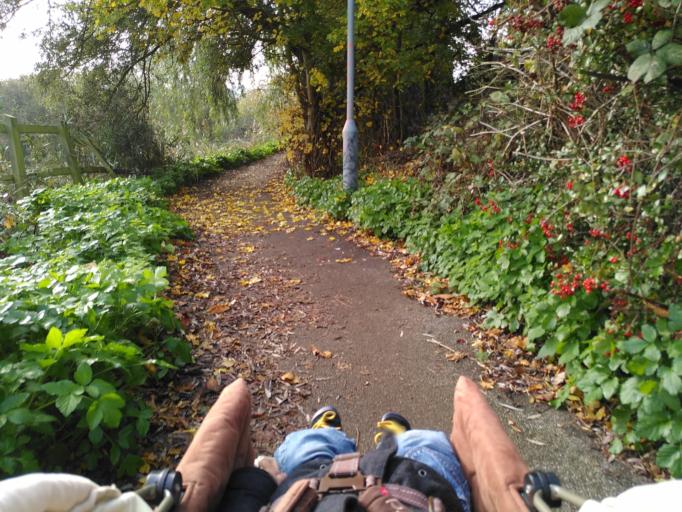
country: GB
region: England
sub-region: Suffolk
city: Bramford
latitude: 52.0627
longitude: 1.1234
